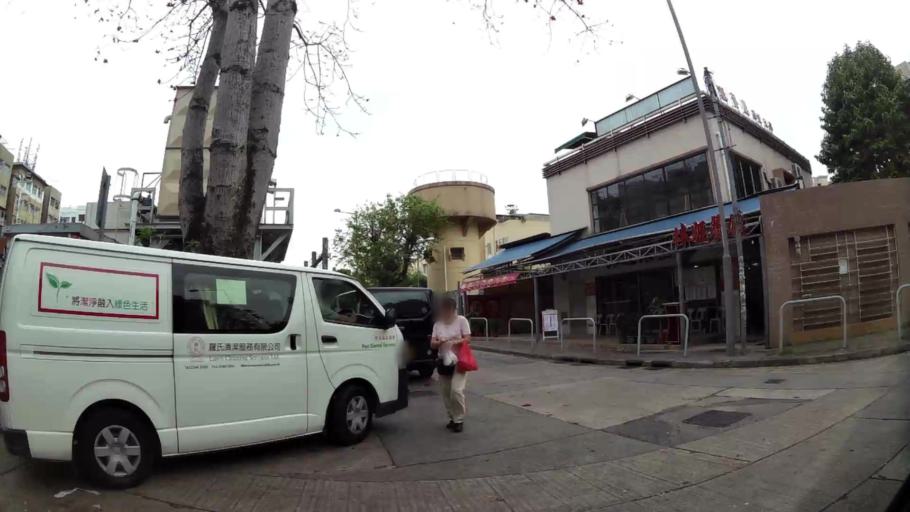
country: HK
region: Yuen Long
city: Yuen Long Kau Hui
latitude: 22.4333
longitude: 113.9958
